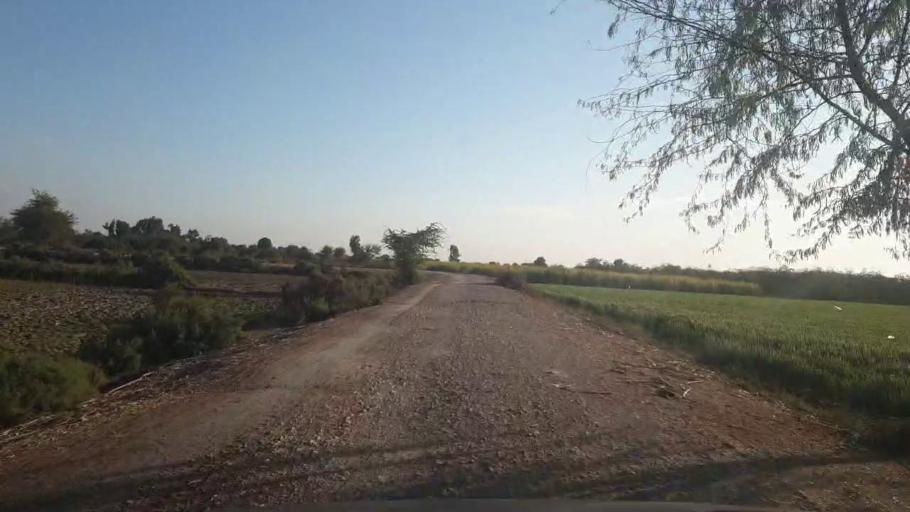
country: PK
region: Sindh
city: Sinjhoro
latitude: 26.0361
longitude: 68.8711
